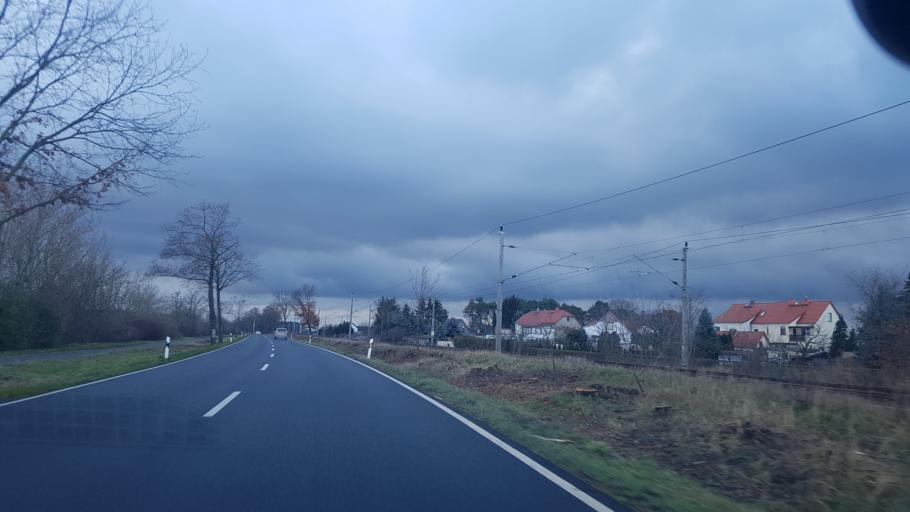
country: DE
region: Brandenburg
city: Merzdorf
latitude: 51.4215
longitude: 13.4991
